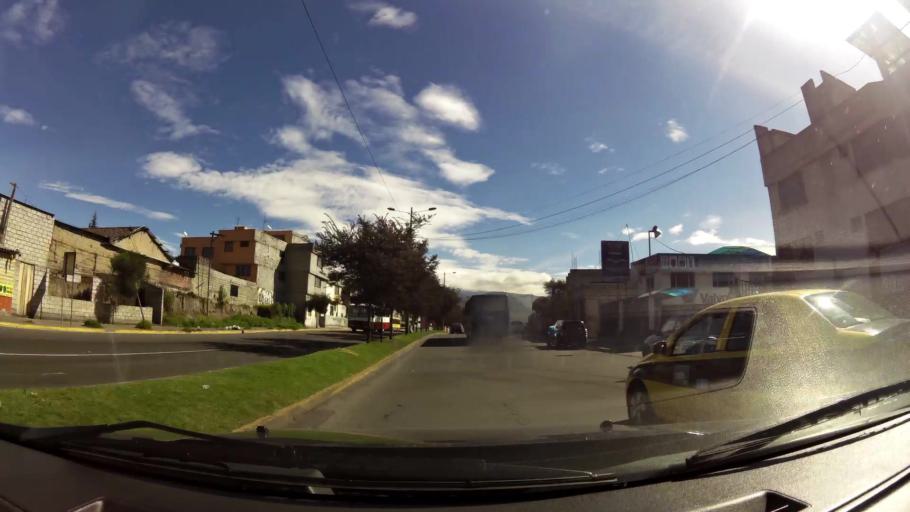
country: EC
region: Pichincha
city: Quito
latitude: -0.2965
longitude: -78.5588
